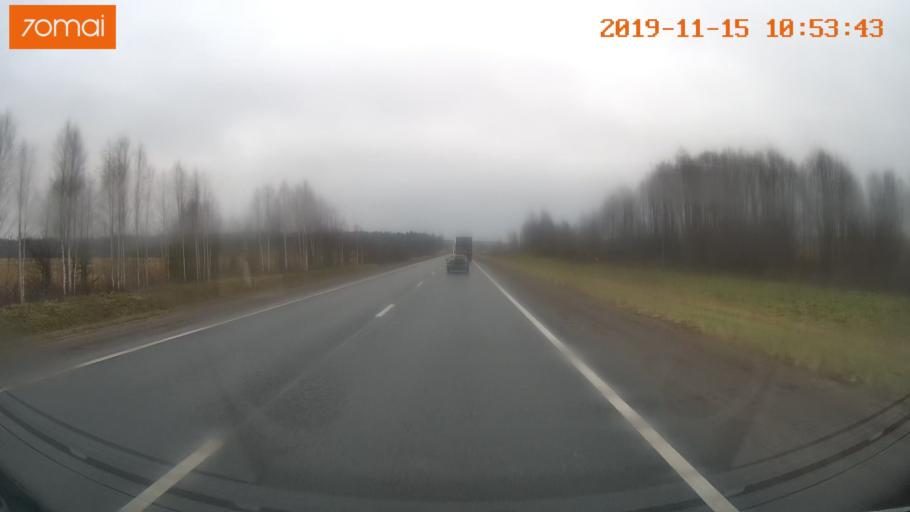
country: RU
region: Vologda
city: Chebsara
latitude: 59.1678
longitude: 38.7606
